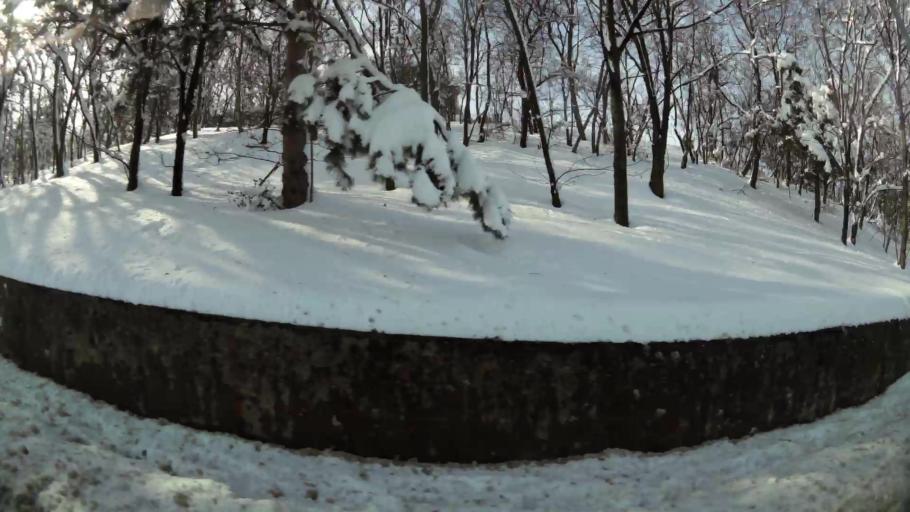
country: RS
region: Central Serbia
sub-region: Belgrade
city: Zvezdara
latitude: 44.7878
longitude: 20.5273
